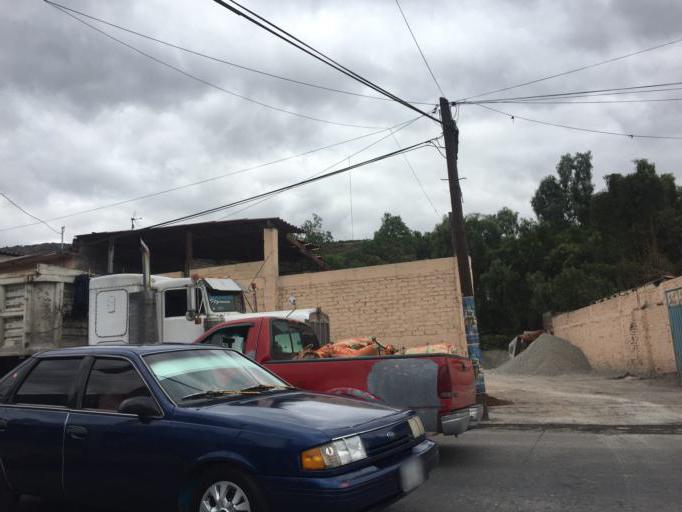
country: MX
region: Mexico
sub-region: Tlalnepantla de Baz
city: Puerto Escondido (Tepeolulco Puerto Escondido)
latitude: 19.5576
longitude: -99.0815
